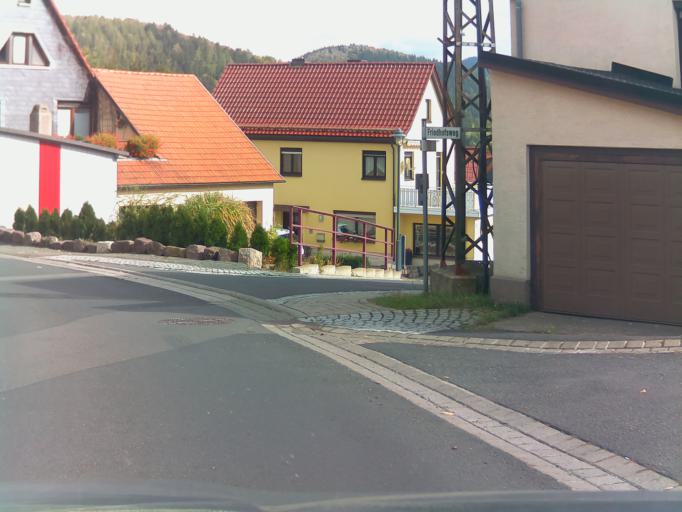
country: DE
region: Thuringia
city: Rotterode
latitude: 50.7116
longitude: 10.5515
